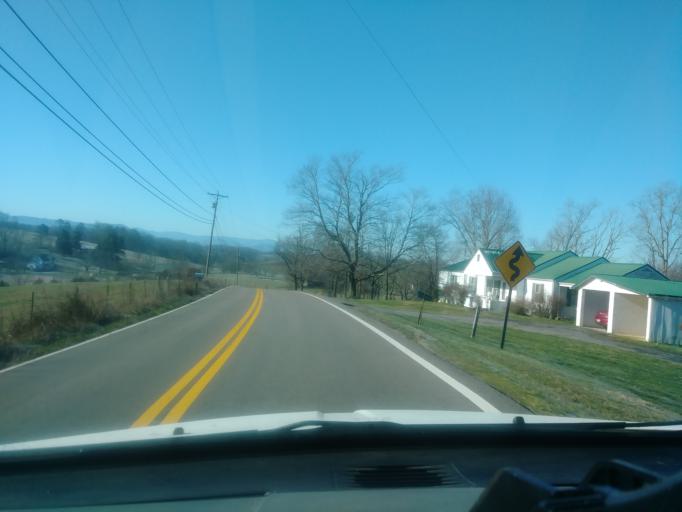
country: US
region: Tennessee
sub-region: Greene County
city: Mosheim
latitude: 36.1155
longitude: -82.9472
